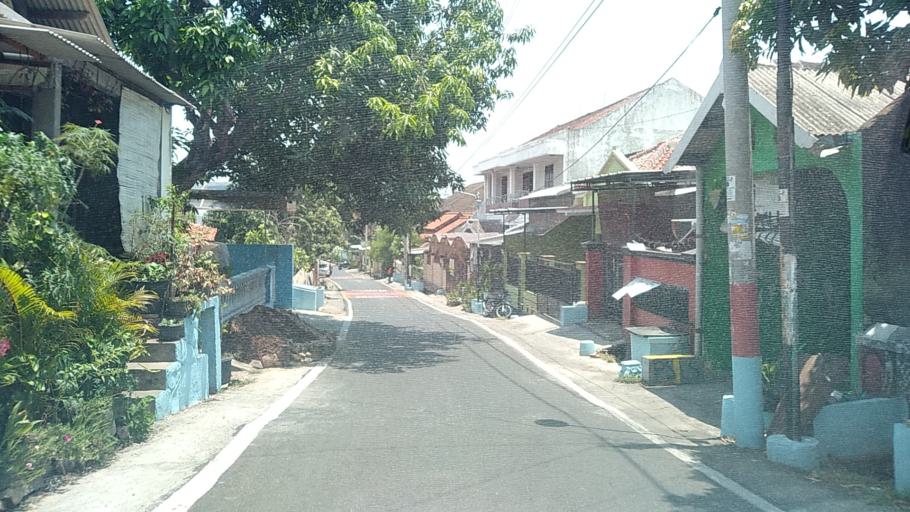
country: ID
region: Central Java
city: Semarang
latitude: -7.0122
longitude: 110.4499
